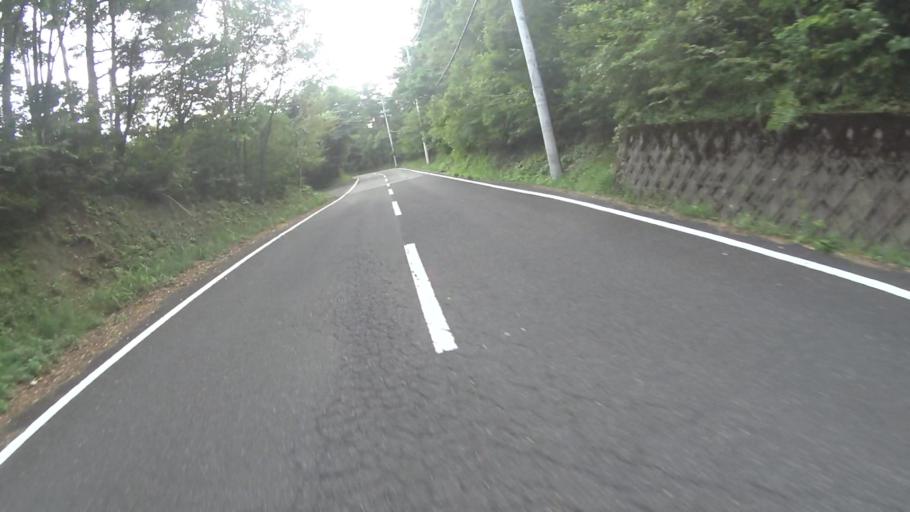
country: JP
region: Kyoto
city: Miyazu
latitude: 35.7328
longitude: 135.1808
